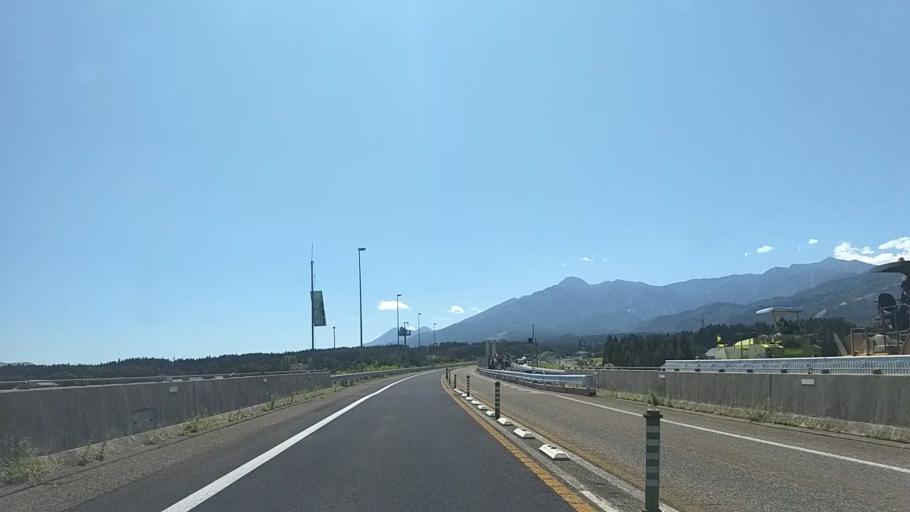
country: JP
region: Niigata
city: Arai
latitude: 37.0134
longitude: 138.2142
